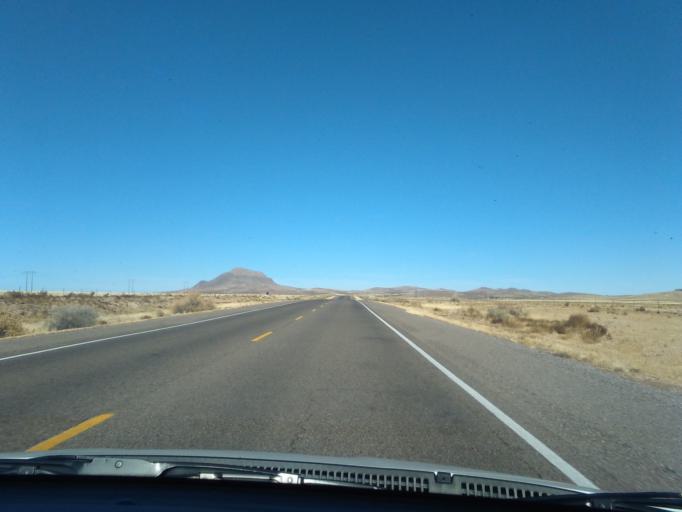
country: US
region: New Mexico
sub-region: Dona Ana County
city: Hatch
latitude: 32.5515
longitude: -107.4763
